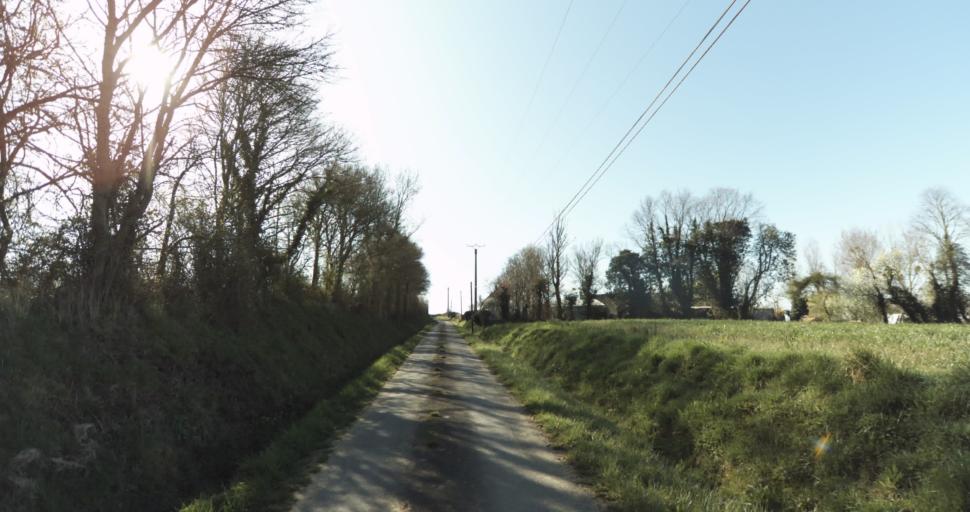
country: FR
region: Lower Normandy
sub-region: Departement du Calvados
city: Saint-Pierre-sur-Dives
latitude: 48.9875
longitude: 0.0130
